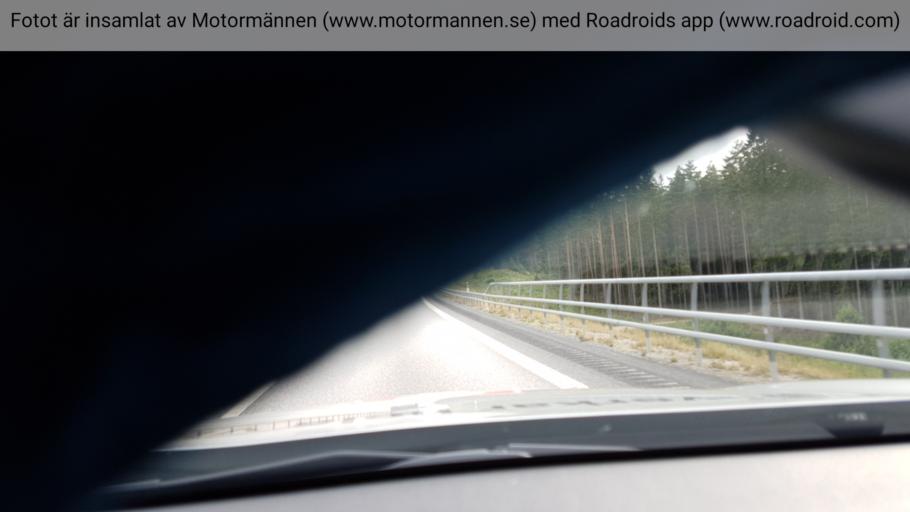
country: SE
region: Vaestra Goetaland
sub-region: Tanums Kommun
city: Tanumshede
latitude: 58.6818
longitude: 11.4099
